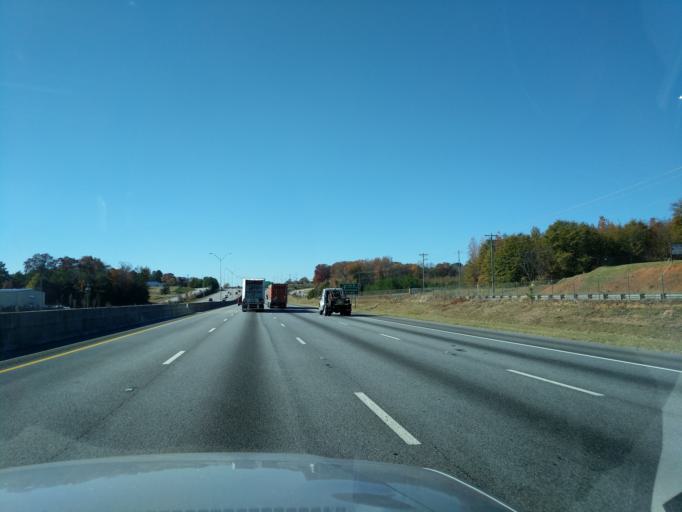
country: US
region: South Carolina
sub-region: Greenville County
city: Gantt
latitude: 34.7928
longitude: -82.4043
